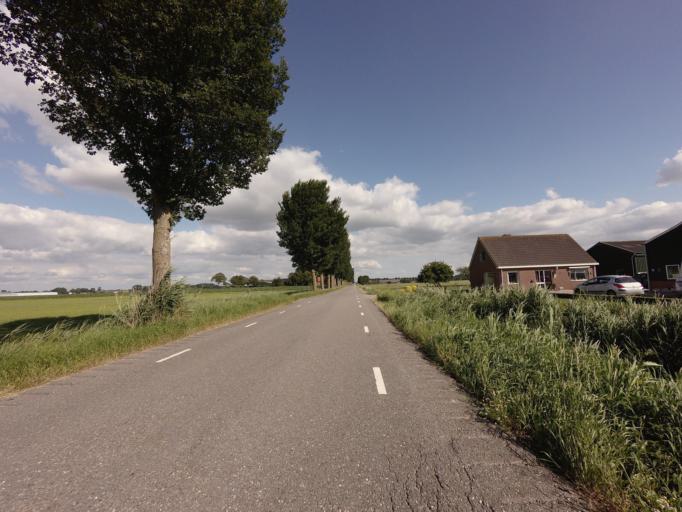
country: NL
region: North Holland
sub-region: Gemeente Uithoorn
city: Uithoorn
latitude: 52.2062
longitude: 4.8206
